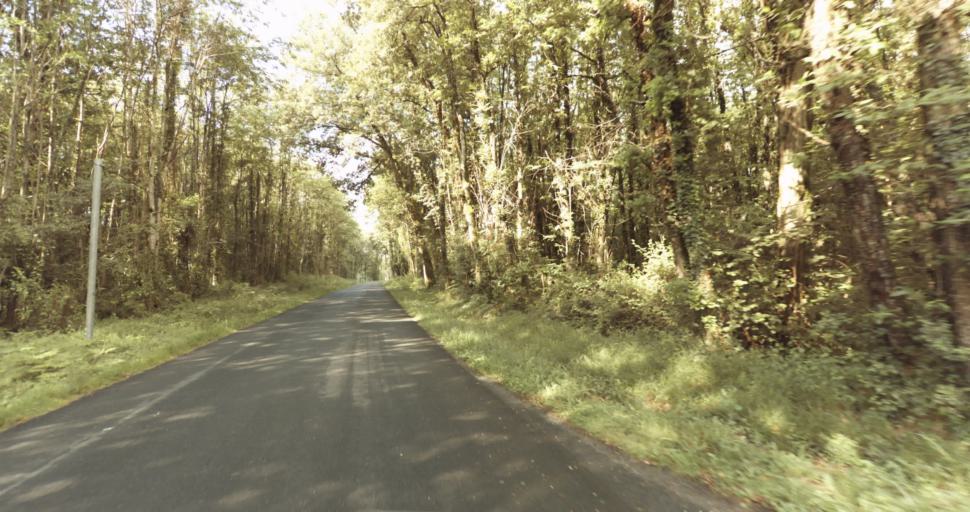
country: FR
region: Aquitaine
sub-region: Departement de la Dordogne
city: Lalinde
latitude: 44.9064
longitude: 0.7808
